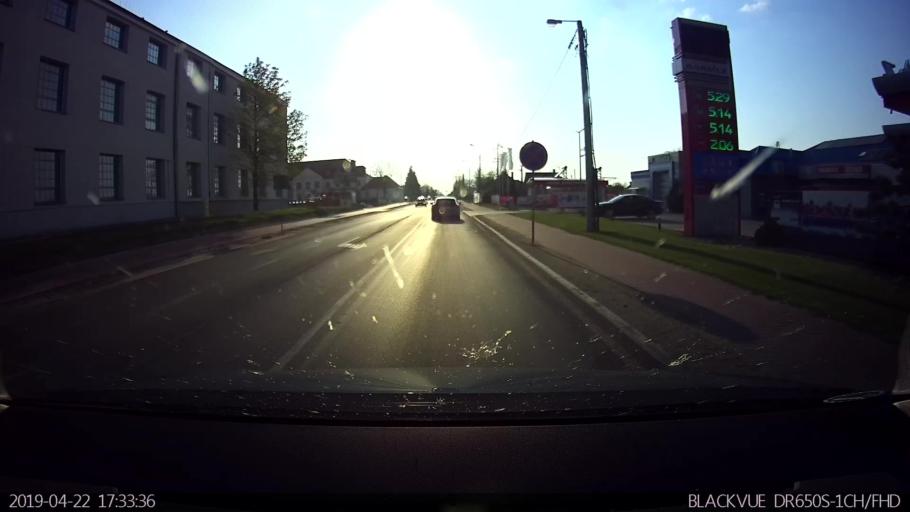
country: PL
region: Masovian Voivodeship
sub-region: Powiat sokolowski
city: Sokolow Podlaski
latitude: 52.4073
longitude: 22.2200
